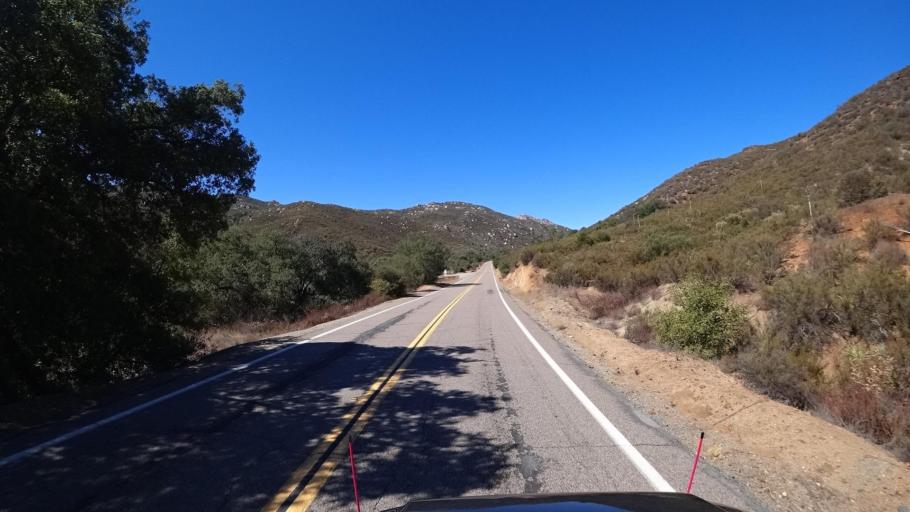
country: US
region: California
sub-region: San Diego County
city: Alpine
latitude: 32.7047
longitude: -116.7186
